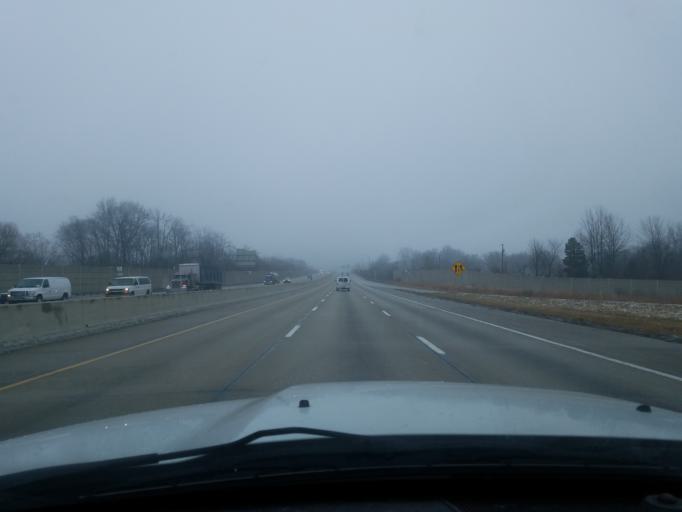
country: US
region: Indiana
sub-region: Marion County
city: Warren Park
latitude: 39.7755
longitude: -86.0307
